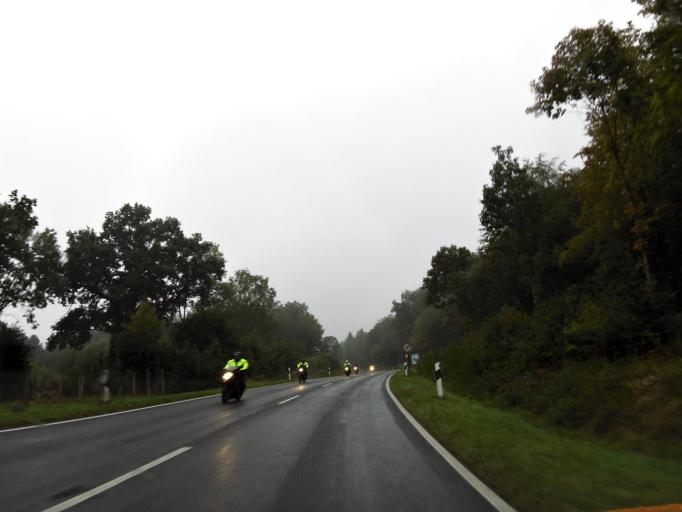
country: DE
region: Lower Saxony
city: Walkenried
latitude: 51.5976
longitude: 10.6004
